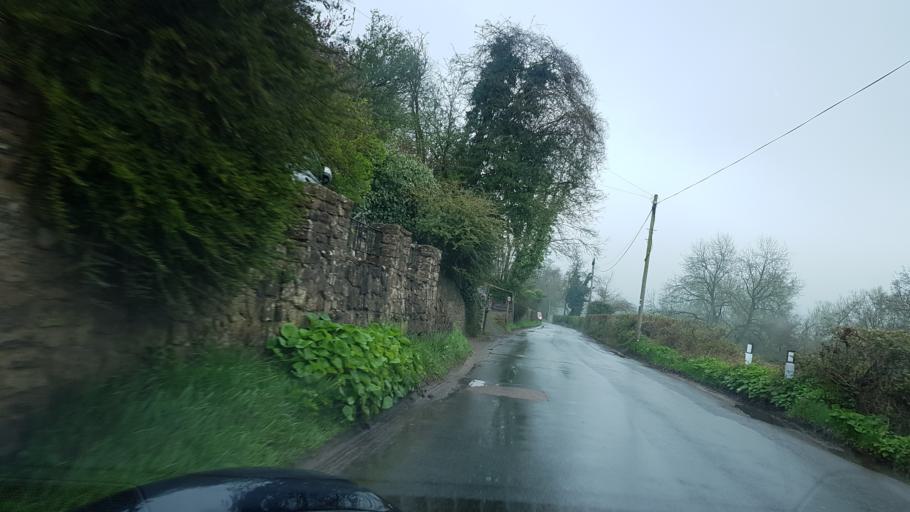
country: GB
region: England
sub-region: Herefordshire
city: Sellack
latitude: 51.9513
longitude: -2.6596
